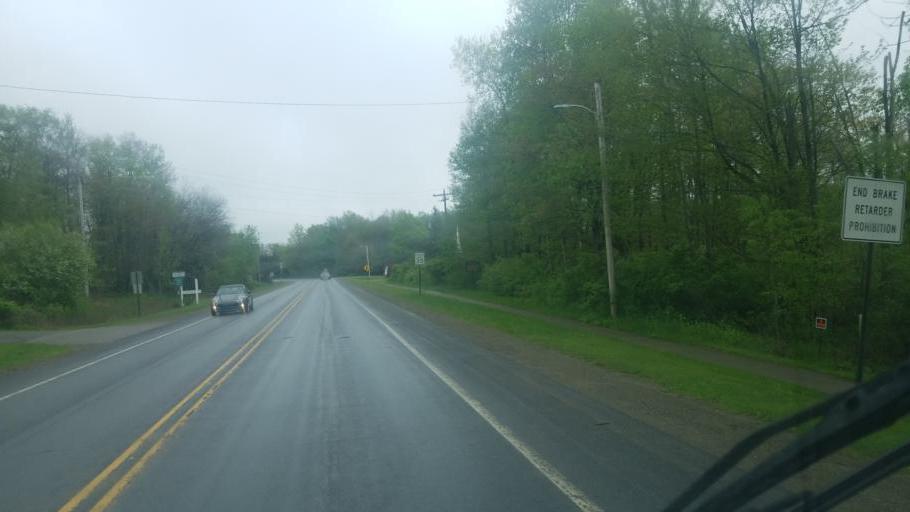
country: US
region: Pennsylvania
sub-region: McKean County
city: Kane
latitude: 41.6583
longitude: -78.8005
